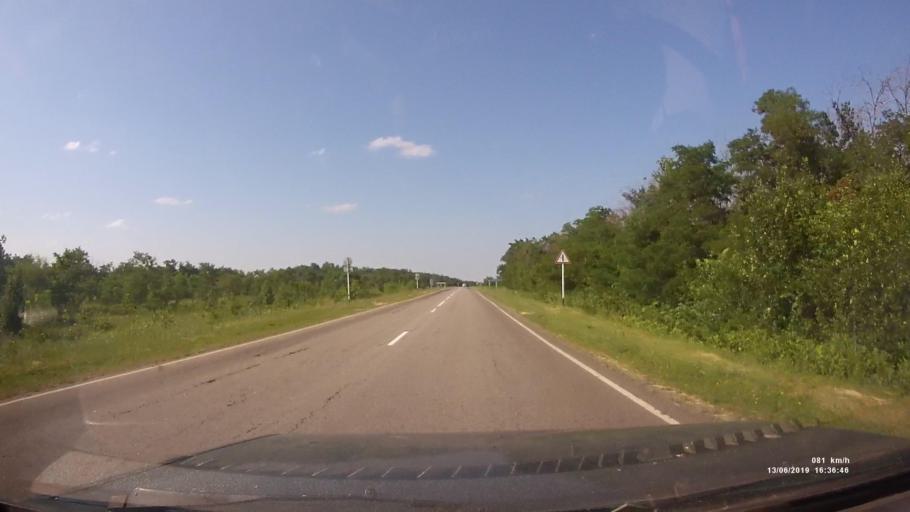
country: RU
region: Rostov
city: Kazanskaya
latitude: 49.8991
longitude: 41.3081
